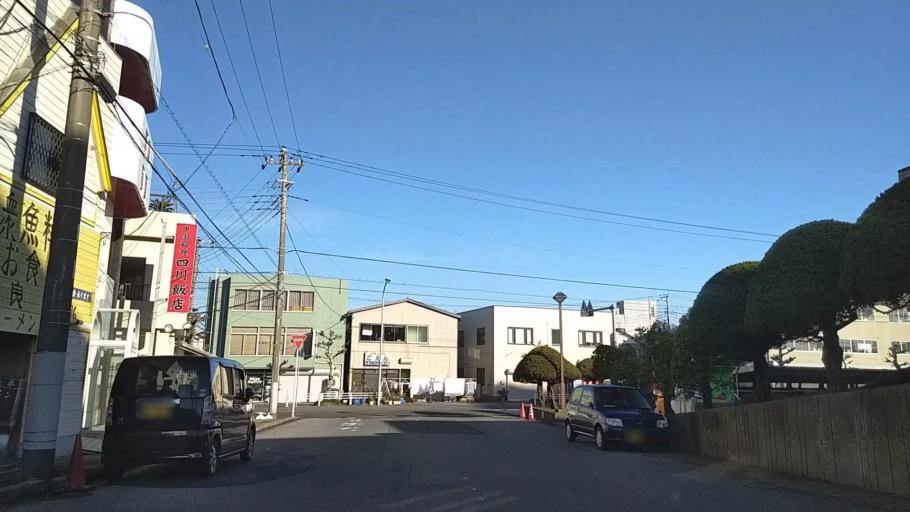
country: JP
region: Chiba
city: Hasaki
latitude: 35.7348
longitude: 140.8260
